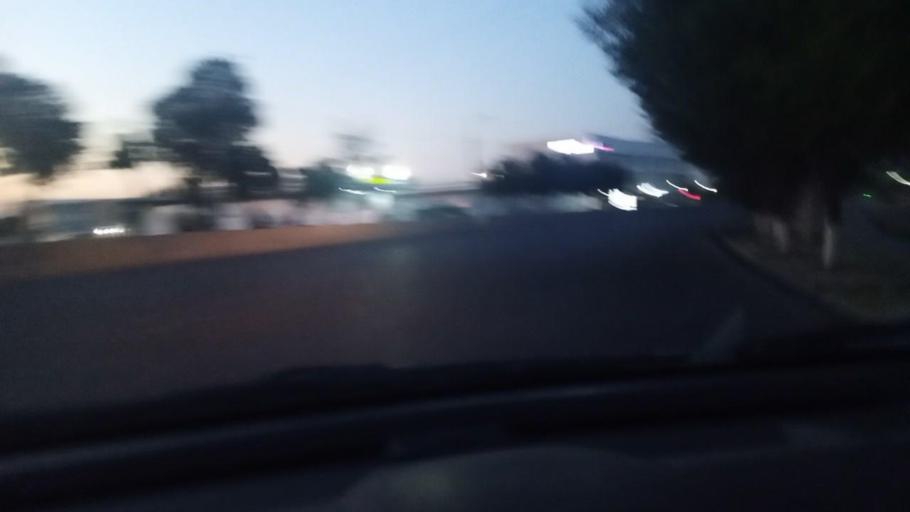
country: UZ
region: Toshkent Shahri
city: Tashkent
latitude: 41.2528
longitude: 69.2169
